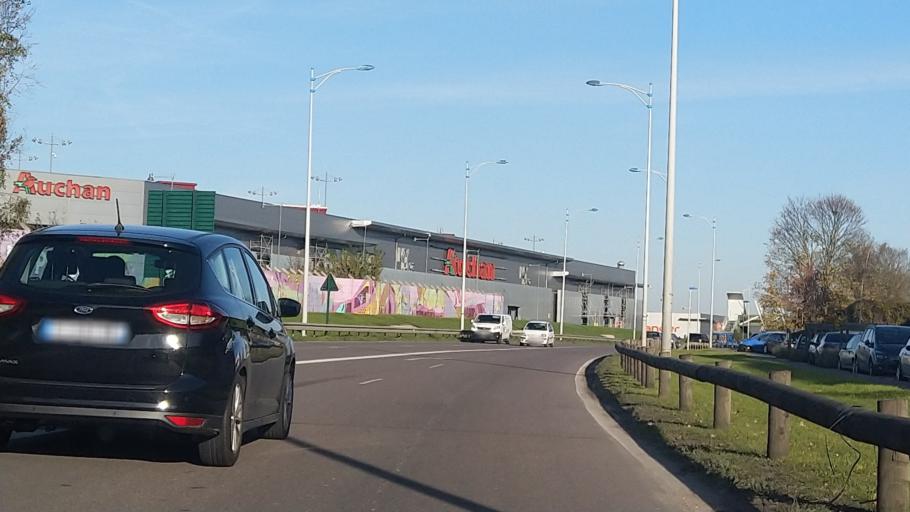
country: FR
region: Ile-de-France
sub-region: Departement de Seine-Saint-Denis
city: Pierrefitte-sur-Seine
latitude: 48.9838
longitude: 2.3717
